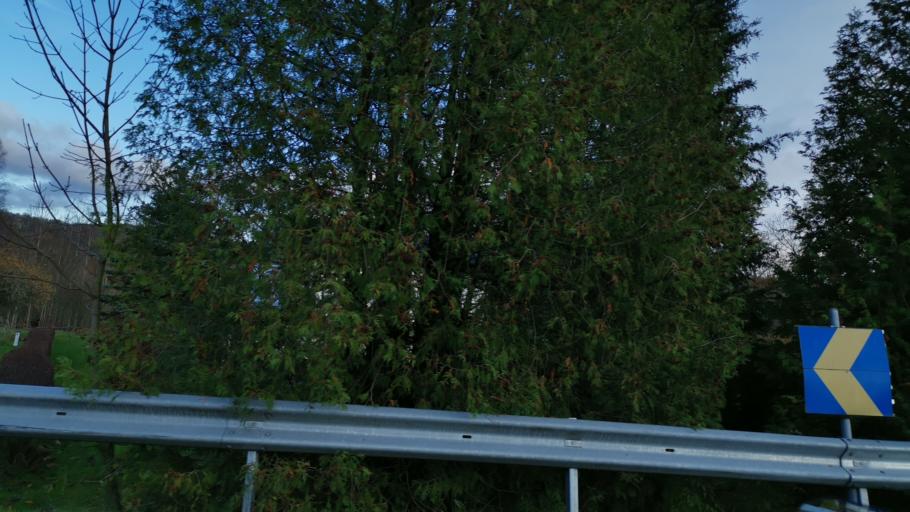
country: SE
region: Vaestra Goetaland
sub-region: Munkedals Kommun
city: Munkedal
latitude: 58.4627
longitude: 11.6788
